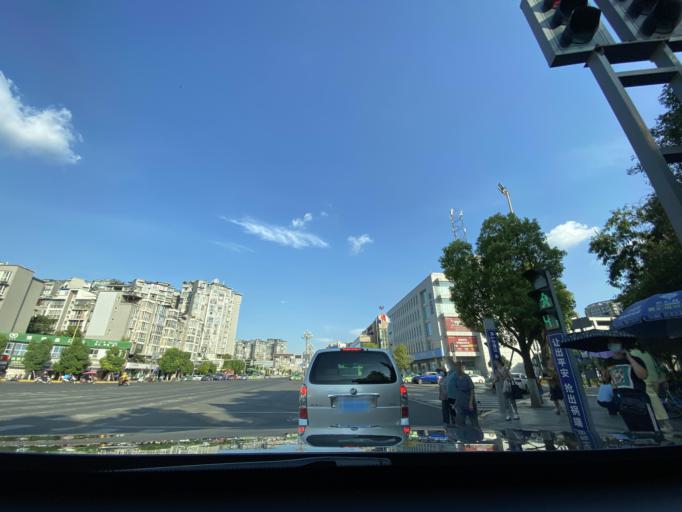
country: CN
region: Sichuan
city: Jiancheng
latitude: 30.4110
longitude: 104.5378
